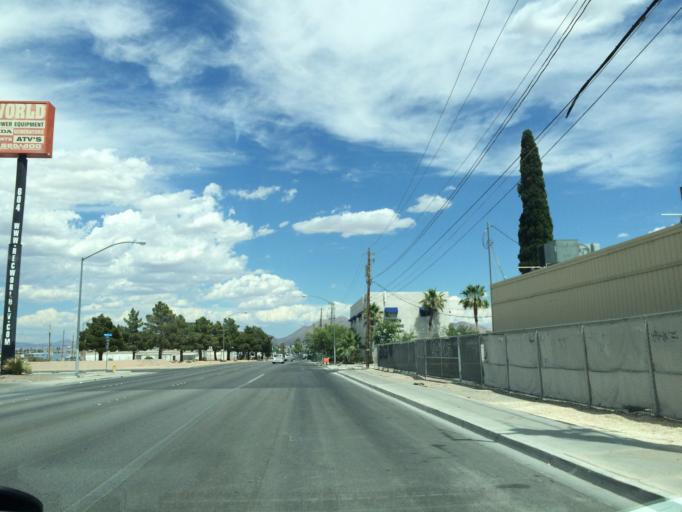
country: US
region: Nevada
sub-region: Clark County
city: North Las Vegas
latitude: 36.1958
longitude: -115.1328
